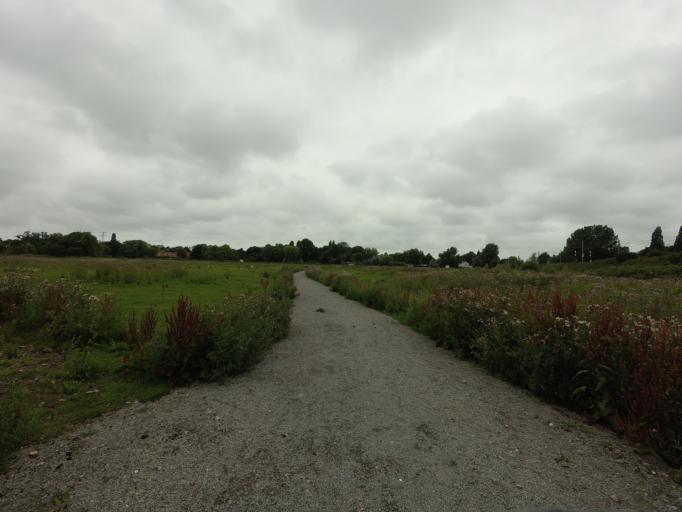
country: NL
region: South Holland
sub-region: Gemeente Oegstgeest
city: Oegstgeest
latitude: 52.1870
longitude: 4.4968
